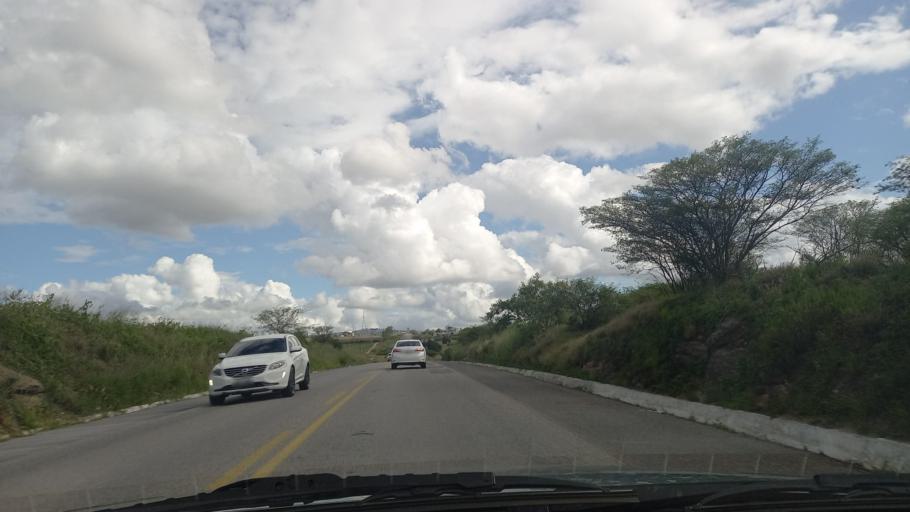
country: BR
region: Pernambuco
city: Garanhuns
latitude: -8.8235
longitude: -36.4492
